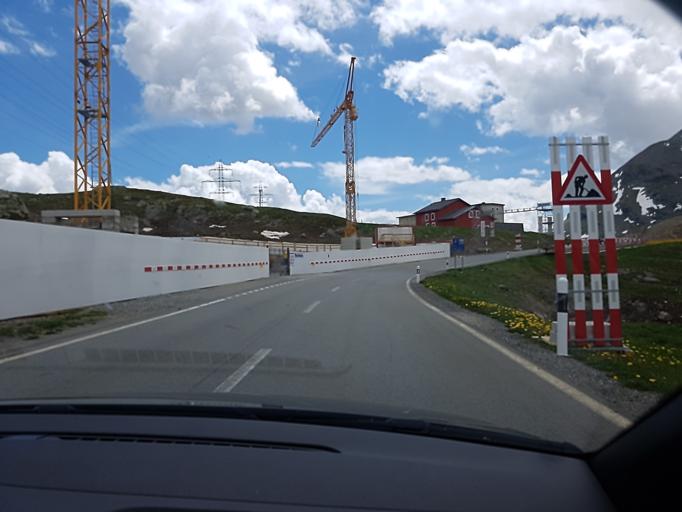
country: CH
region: Grisons
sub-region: Bernina District
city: Poschiavo
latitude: 46.4130
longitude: 10.0212
